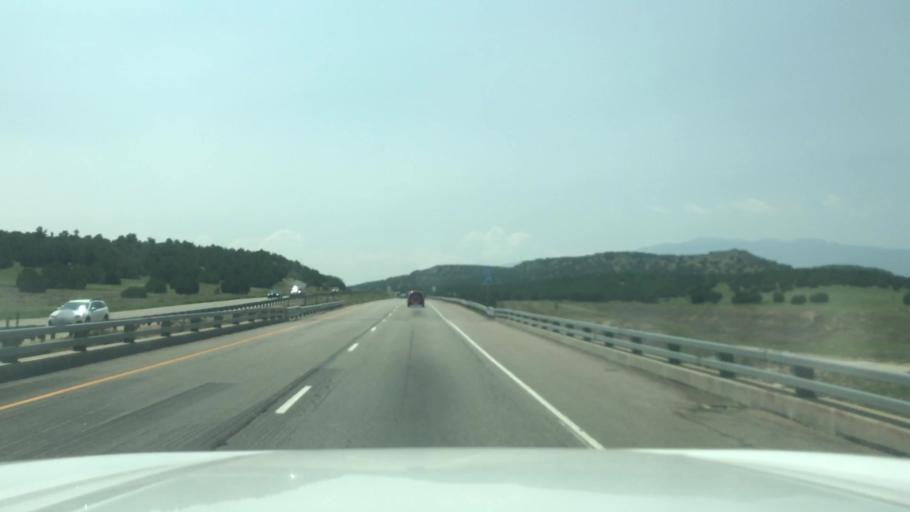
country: US
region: Colorado
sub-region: Pueblo County
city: Colorado City
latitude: 37.9920
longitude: -104.7655
